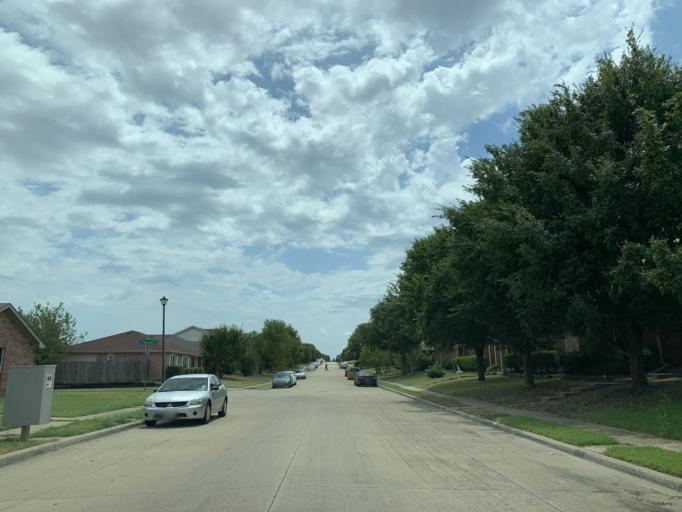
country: US
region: Texas
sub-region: Dallas County
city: DeSoto
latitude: 32.6613
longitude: -96.8114
